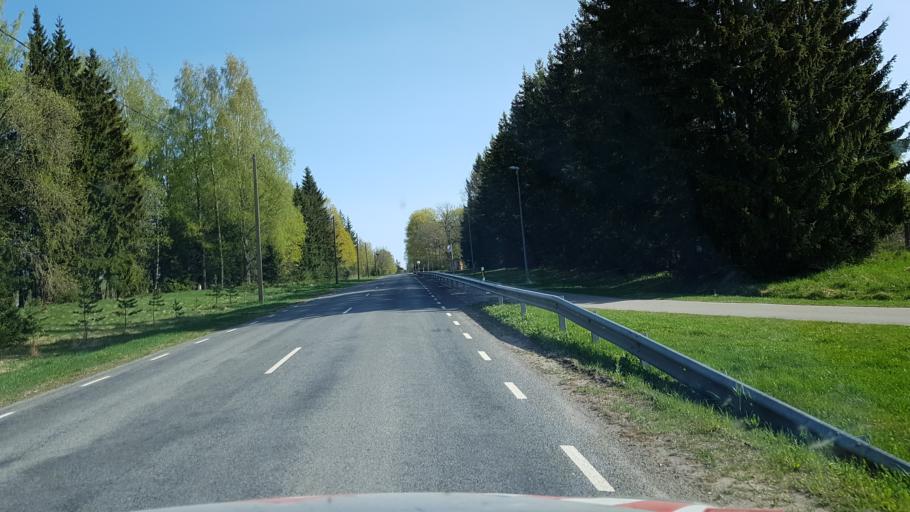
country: EE
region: Viljandimaa
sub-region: Abja vald
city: Abja-Paluoja
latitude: 58.1592
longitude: 25.4342
